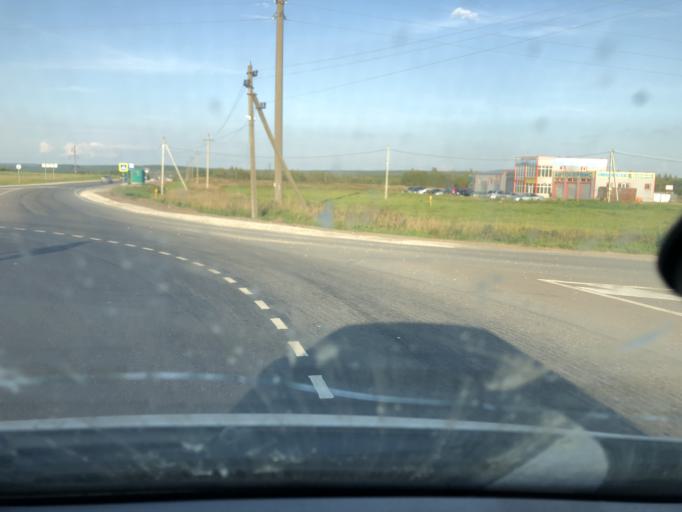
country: RU
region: Kaluga
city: Peremyshl'
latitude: 54.2782
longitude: 36.1434
